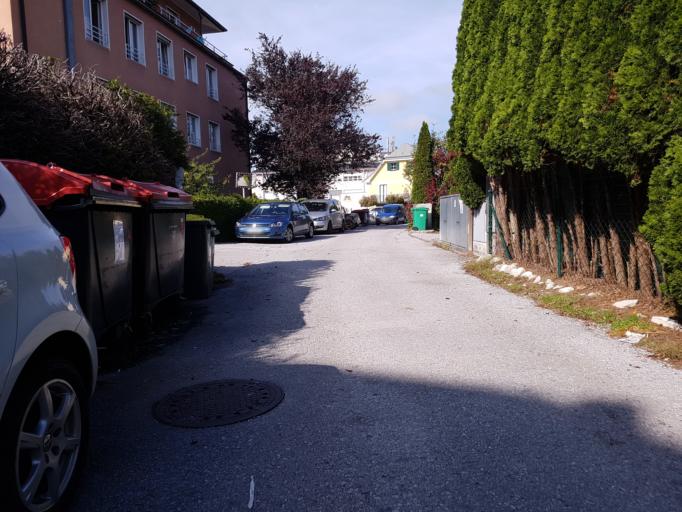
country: AT
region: Salzburg
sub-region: Salzburg Stadt
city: Salzburg
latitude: 47.7850
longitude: 13.0530
